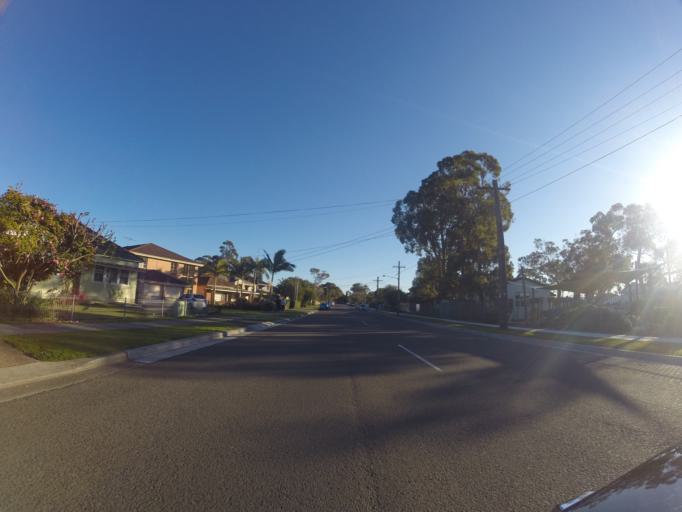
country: AU
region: New South Wales
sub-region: Sutherland Shire
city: Gymea Bay
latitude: -34.0512
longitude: 151.0879
